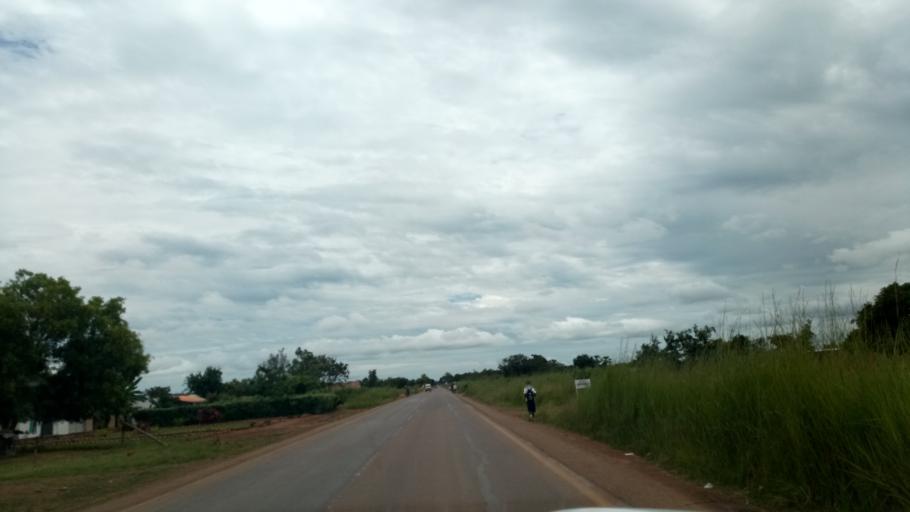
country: CD
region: Katanga
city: Lubumbashi
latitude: -11.5597
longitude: 27.5717
